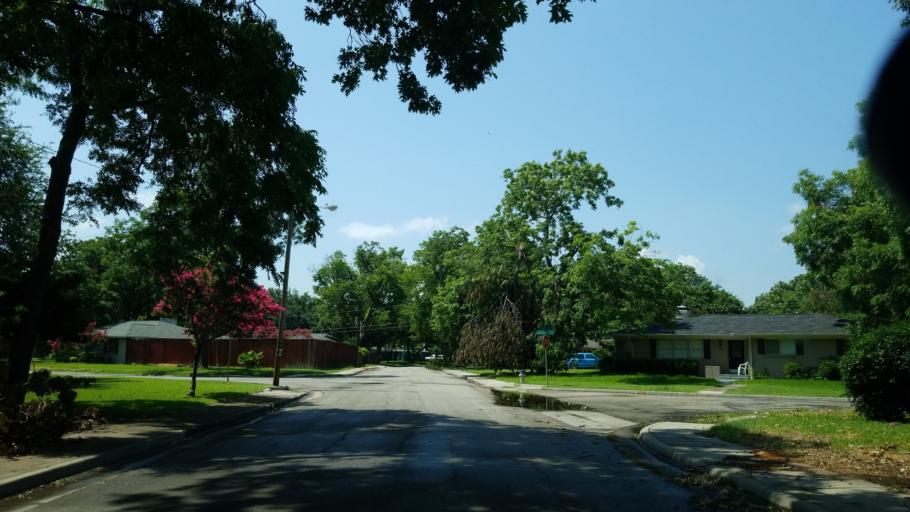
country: US
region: Texas
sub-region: Dallas County
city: Farmers Branch
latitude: 32.8787
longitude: -96.8679
